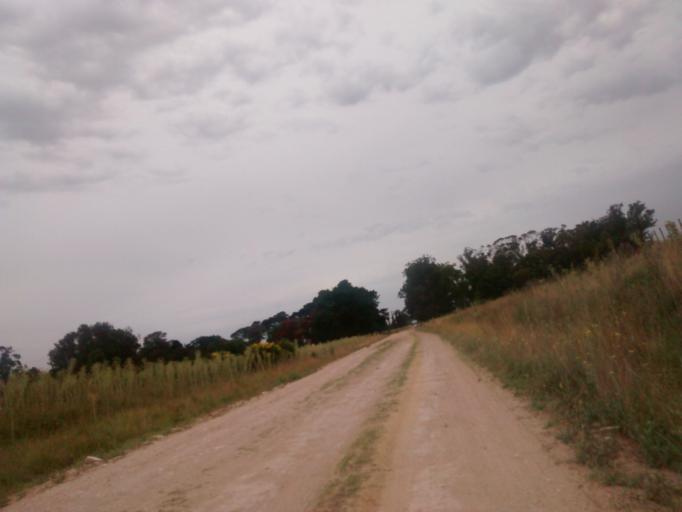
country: AR
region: Buenos Aires
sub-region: Partido de Loberia
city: Loberia
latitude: -38.1891
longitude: -58.7346
